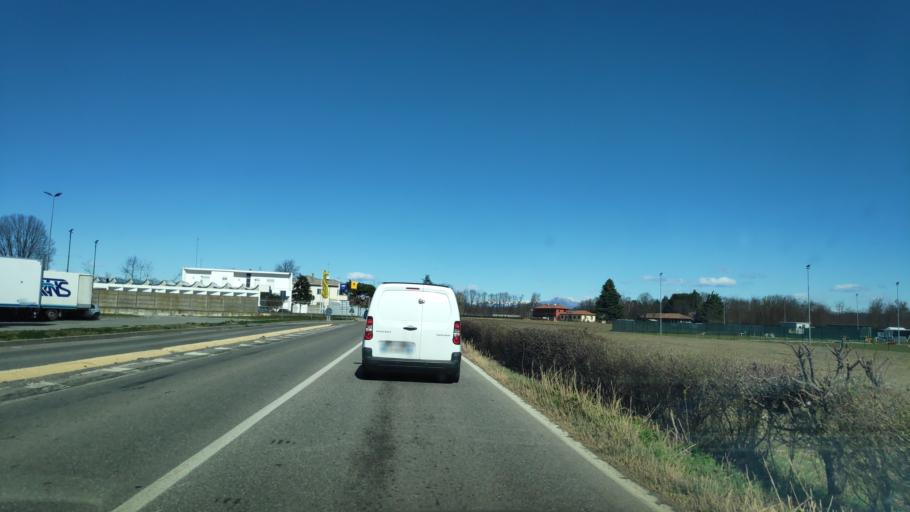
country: IT
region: Lombardy
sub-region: Provincia di Varese
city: Fagnano Olona-Bergoro
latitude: 45.6465
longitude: 8.8471
